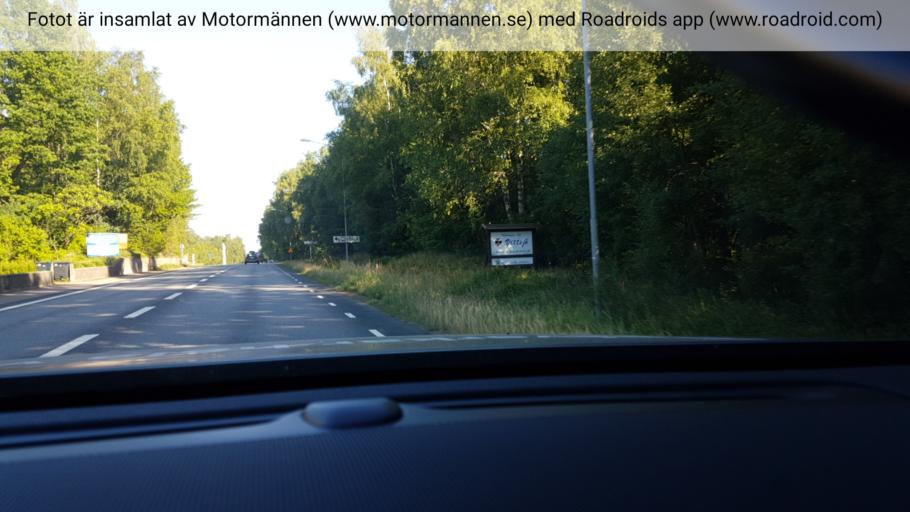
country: SE
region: Skane
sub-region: Hassleholms Kommun
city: Bjarnum
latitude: 56.3312
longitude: 13.6732
